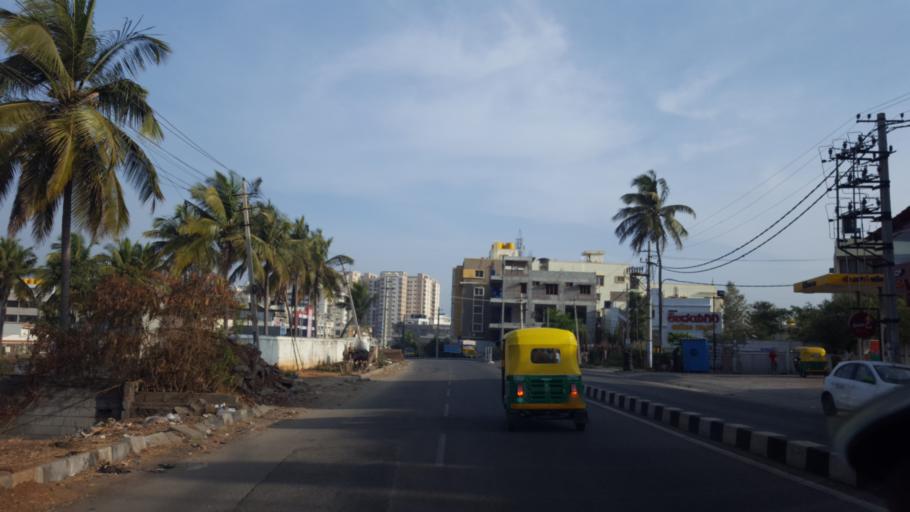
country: IN
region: Karnataka
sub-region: Bangalore Urban
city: Bangalore
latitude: 12.9057
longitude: 77.5124
